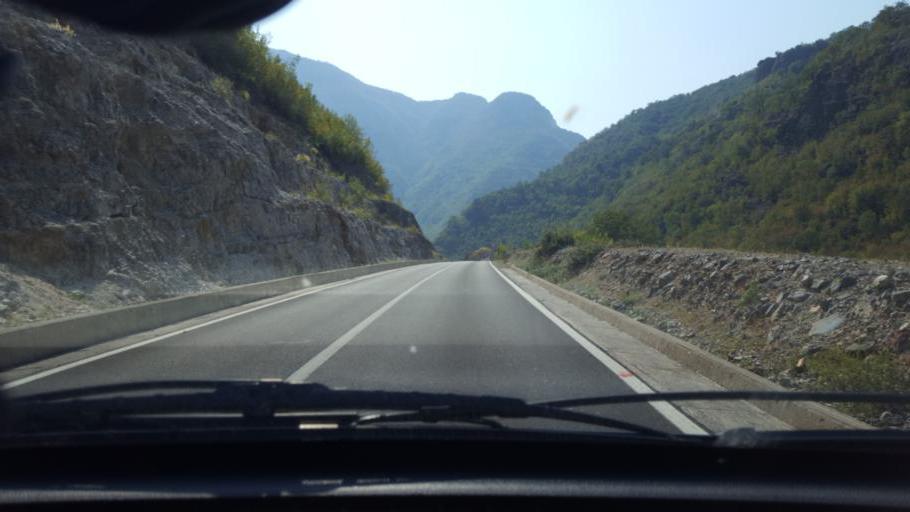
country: AL
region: Shkoder
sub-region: Rrethi i Malesia e Madhe
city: Kastrat
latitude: 42.4357
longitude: 19.5373
